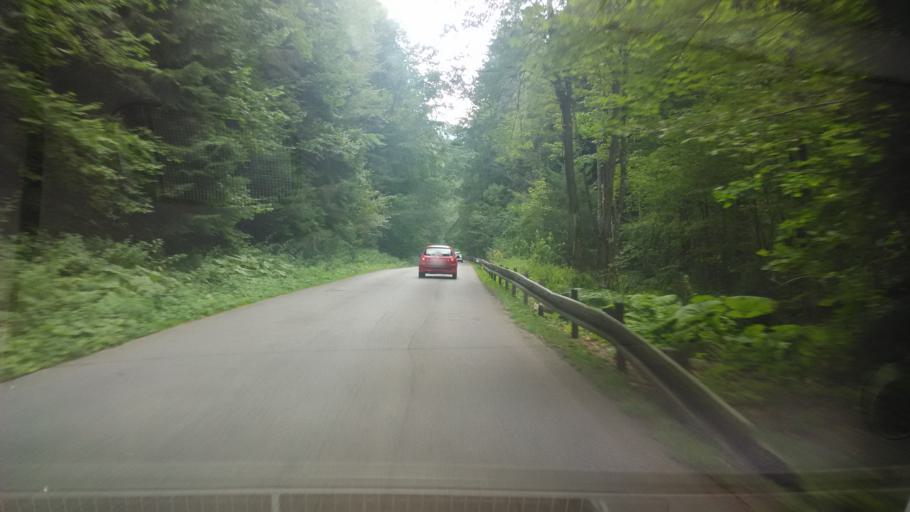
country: SK
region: Banskobystricky
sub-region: Okres Ziar nad Hronom
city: Kremnica
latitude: 48.7138
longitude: 18.9563
